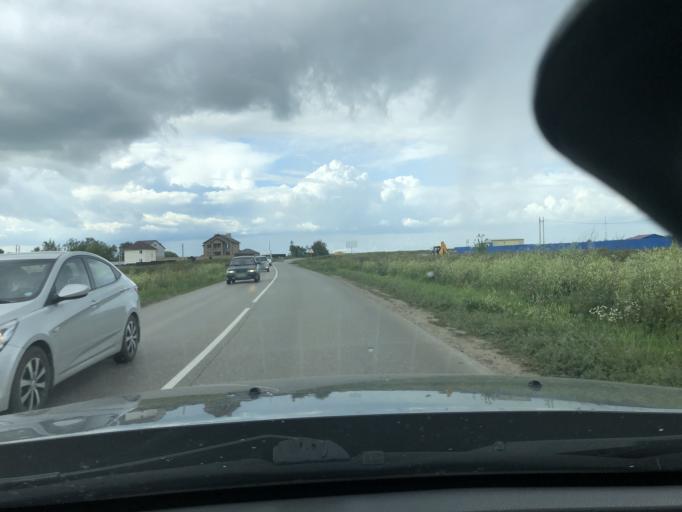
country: RU
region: Tula
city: Kamenetskiy
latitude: 54.0109
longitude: 38.2526
